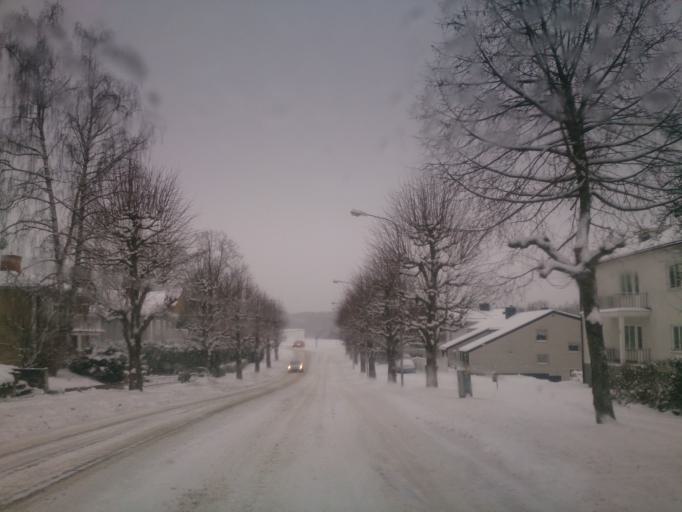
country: SE
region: OEstergoetland
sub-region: Finspangs Kommun
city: Finspang
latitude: 58.7063
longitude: 15.7896
